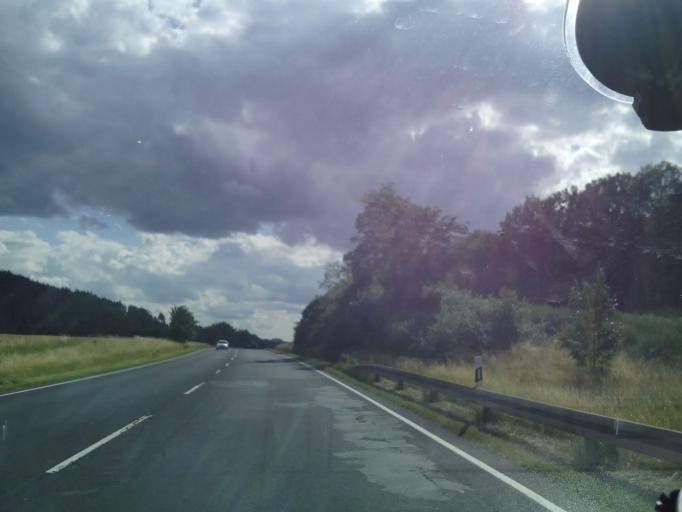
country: DE
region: Bavaria
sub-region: Upper Franconia
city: Rodental
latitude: 50.3111
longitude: 11.0773
